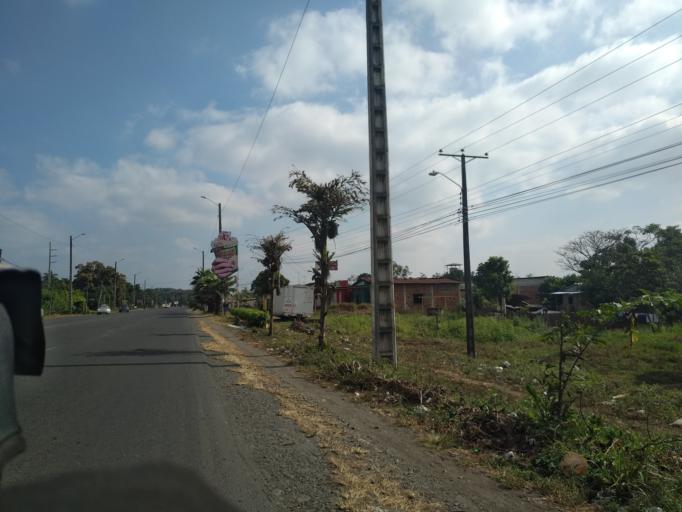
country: EC
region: Los Rios
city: Quevedo
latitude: -1.0623
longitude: -79.4907
